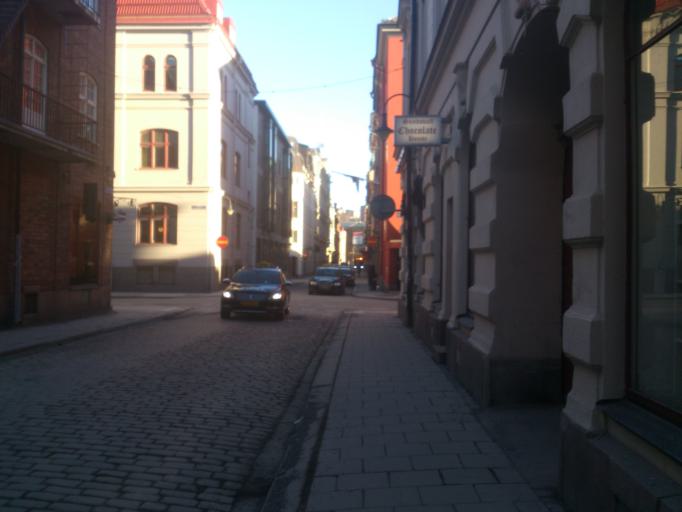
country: SE
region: Vaesternorrland
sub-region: Sundsvalls Kommun
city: Sundsvall
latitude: 62.3891
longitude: 17.3109
